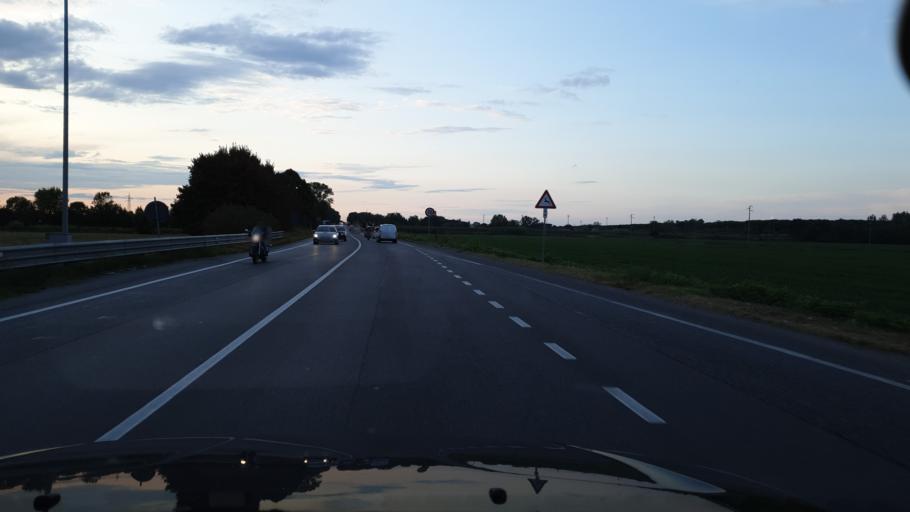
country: IT
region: Emilia-Romagna
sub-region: Provincia di Ravenna
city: Savio
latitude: 44.3209
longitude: 12.2829
